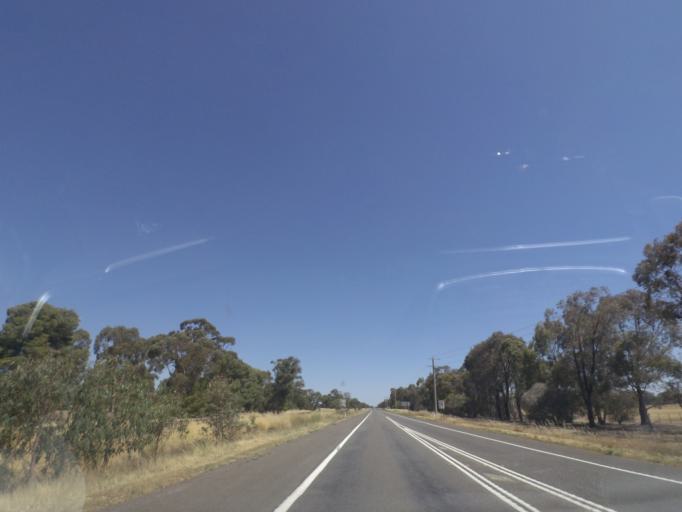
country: AU
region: Victoria
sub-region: Greater Shepparton
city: Shepparton
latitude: -36.2406
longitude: 145.4318
